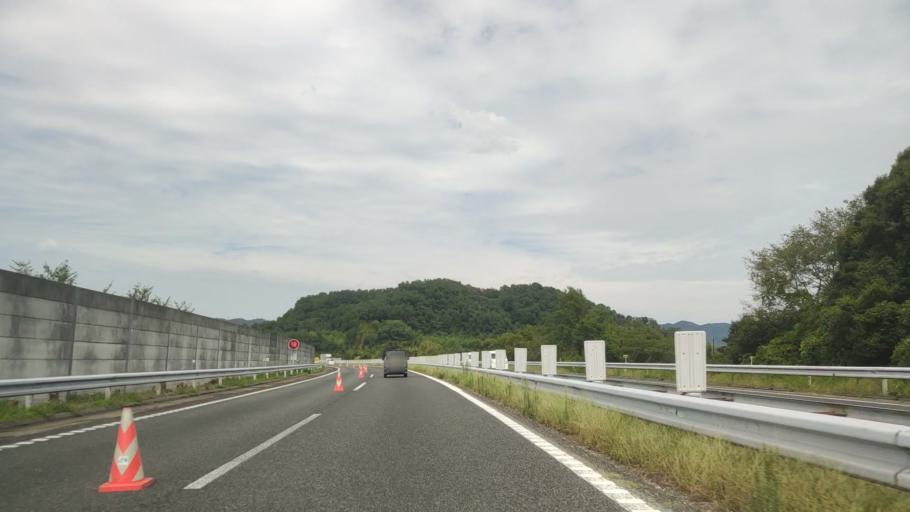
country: JP
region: Wakayama
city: Kainan
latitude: 34.1883
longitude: 135.2387
